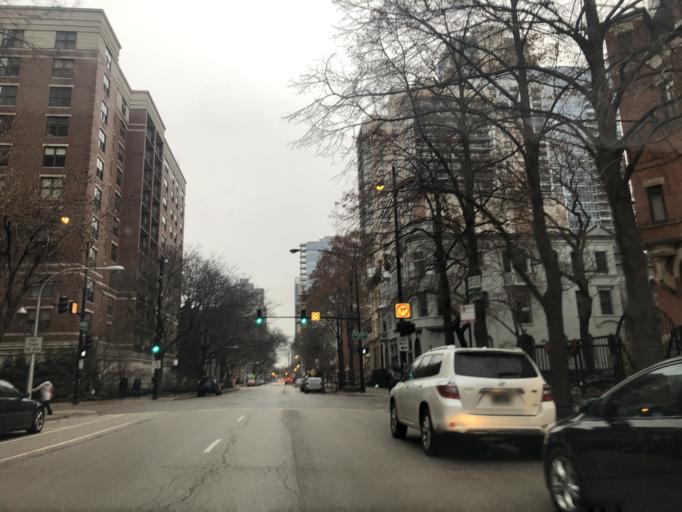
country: US
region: Illinois
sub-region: Cook County
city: Chicago
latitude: 41.8976
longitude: -87.6298
